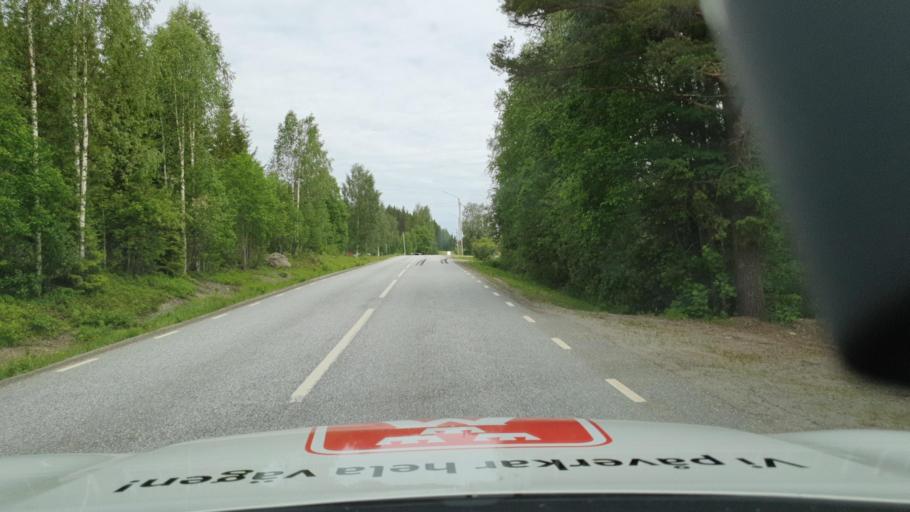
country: SE
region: Vaesterbotten
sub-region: Umea Kommun
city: Ersmark
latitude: 64.3056
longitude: 20.2215
